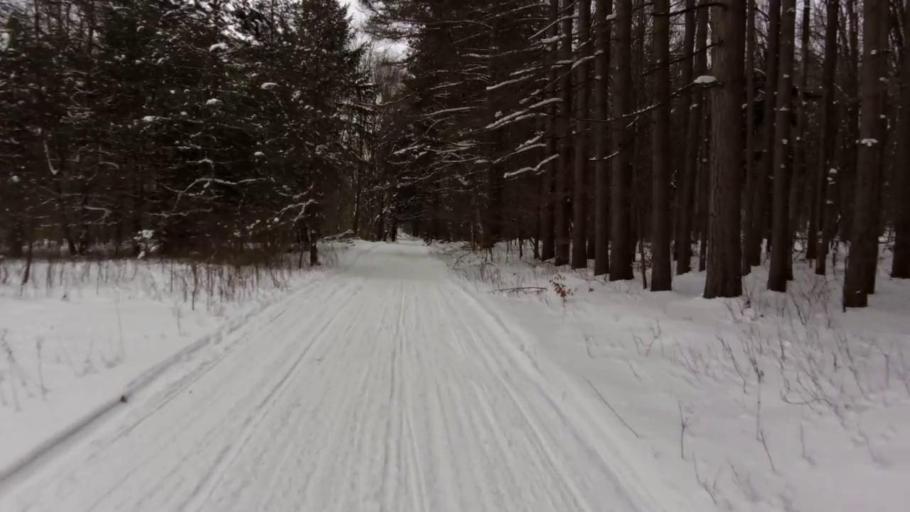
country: US
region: Pennsylvania
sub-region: McKean County
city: Bradford
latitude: 42.0245
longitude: -78.7220
